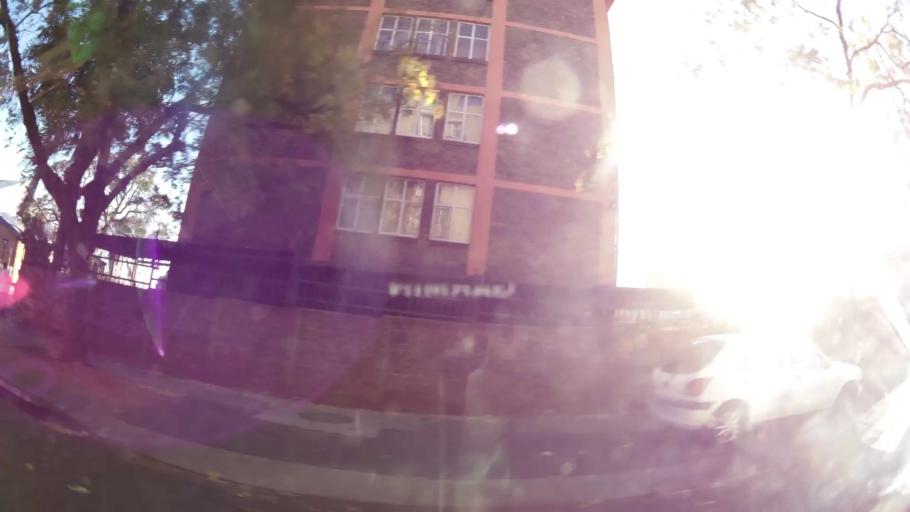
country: ZA
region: Gauteng
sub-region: City of Tshwane Metropolitan Municipality
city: Pretoria
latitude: -25.6985
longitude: 28.2007
